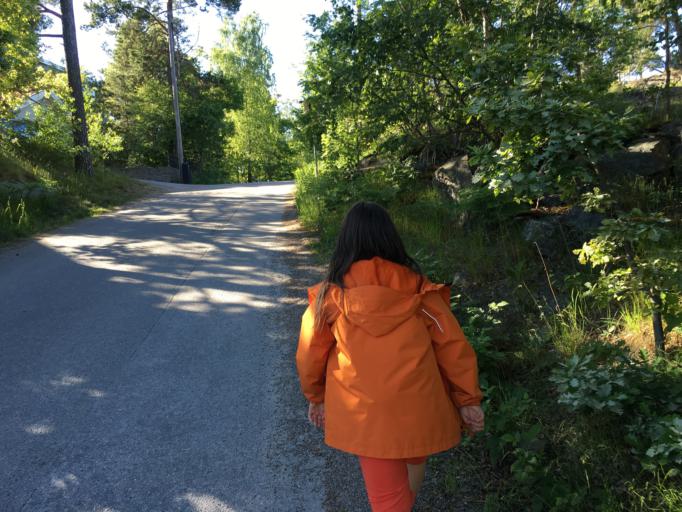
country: SE
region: Stockholm
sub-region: Nacka Kommun
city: Boo
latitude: 59.3210
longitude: 18.2417
